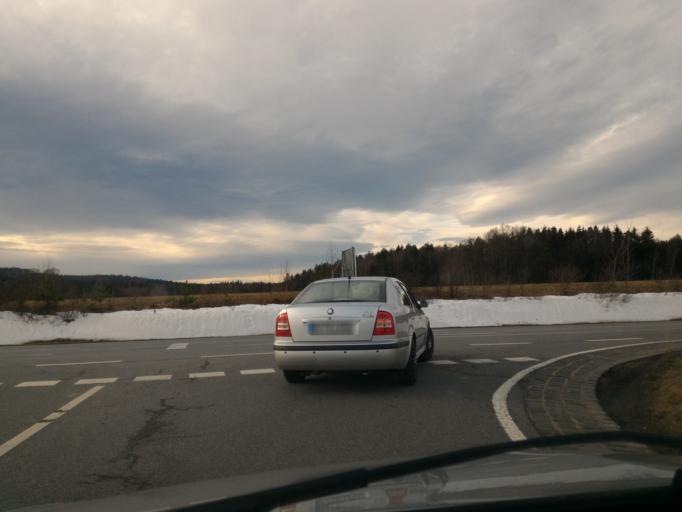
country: DE
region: Saxony
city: Bischofswerda
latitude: 51.1049
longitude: 14.1935
